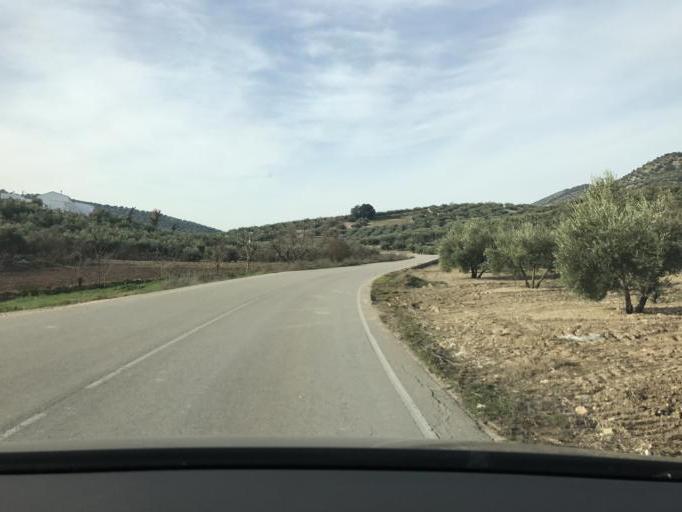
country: ES
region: Andalusia
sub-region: Provincia de Granada
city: Algarinejo
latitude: 37.3187
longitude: -4.1970
